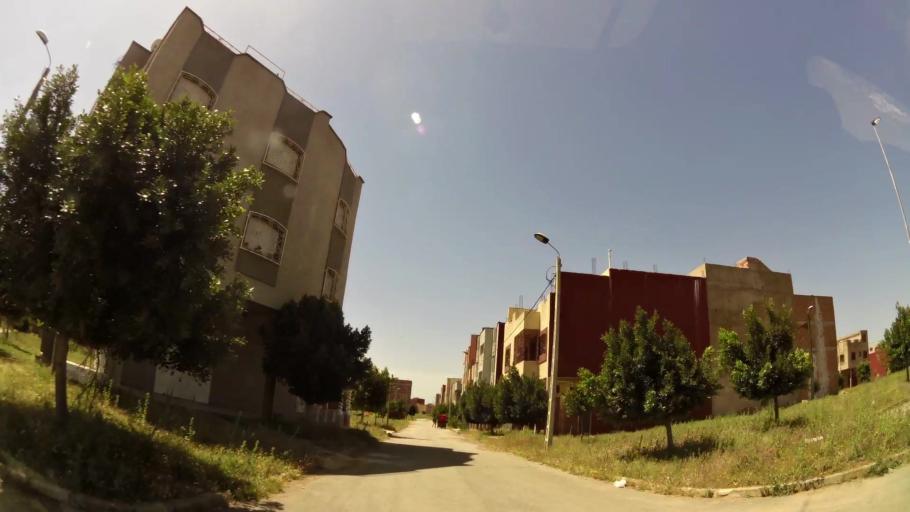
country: MA
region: Rabat-Sale-Zemmour-Zaer
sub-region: Khemisset
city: Khemisset
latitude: 33.8111
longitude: -6.0877
